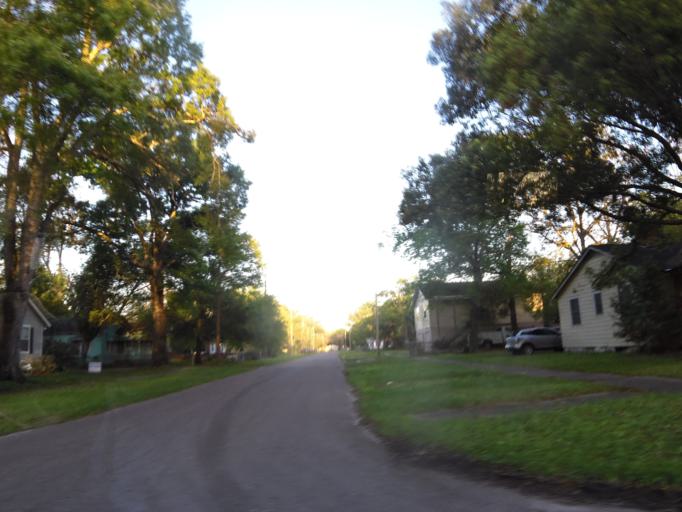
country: US
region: Florida
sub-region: Duval County
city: Jacksonville
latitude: 30.3347
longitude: -81.7130
